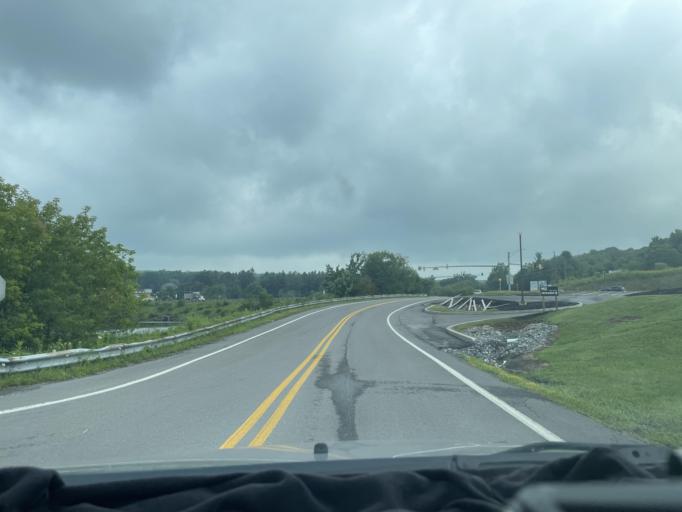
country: US
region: Maryland
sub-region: Garrett County
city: Oakland
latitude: 39.5576
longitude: -79.3534
